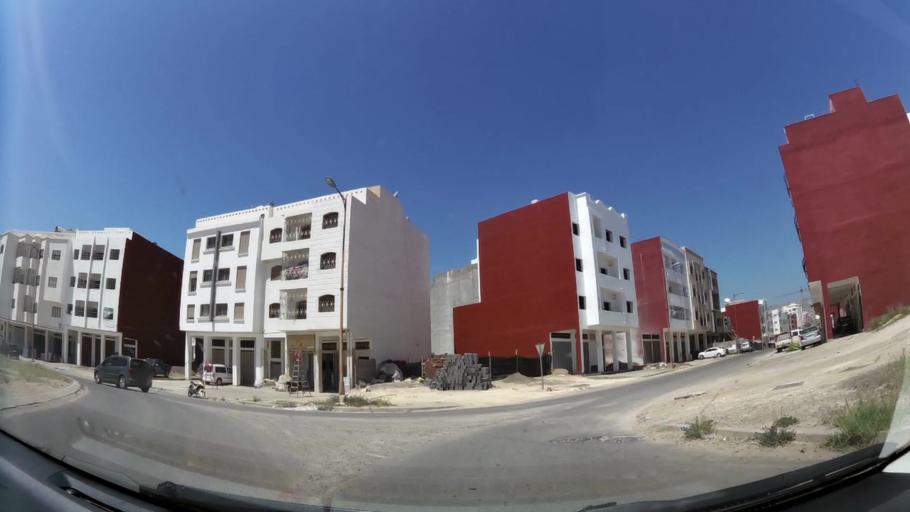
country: MA
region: Oued ed Dahab-Lagouira
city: Dakhla
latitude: 30.4299
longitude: -9.5523
